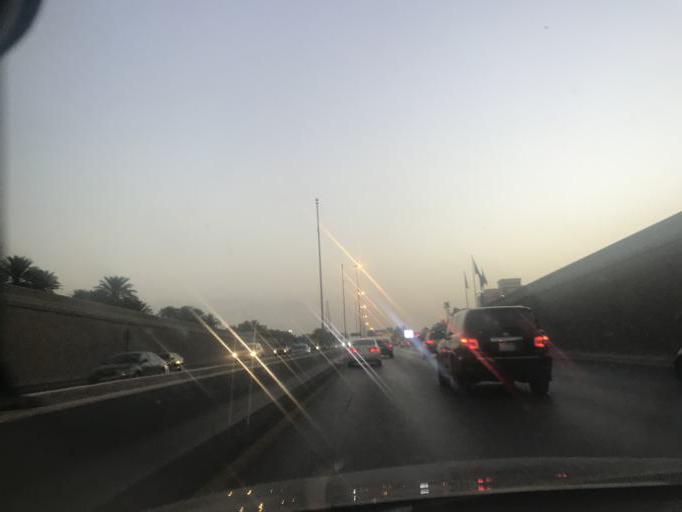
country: SA
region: Ar Riyad
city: Riyadh
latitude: 24.6753
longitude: 46.6770
